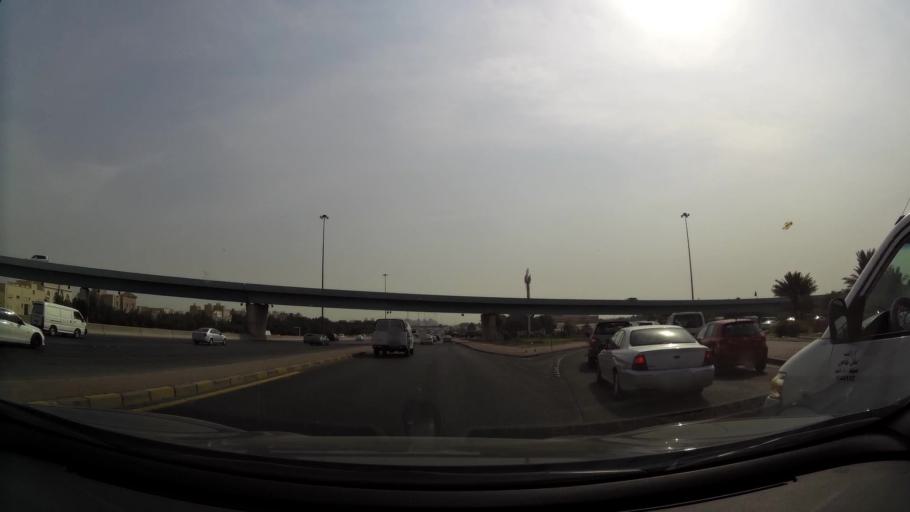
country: KW
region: Al Asimah
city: Ar Rabiyah
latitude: 29.3006
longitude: 47.9453
